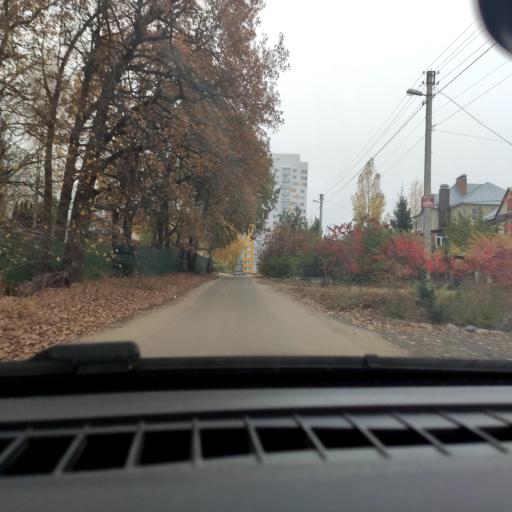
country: RU
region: Voronezj
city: Podgornoye
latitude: 51.7628
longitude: 39.1812
